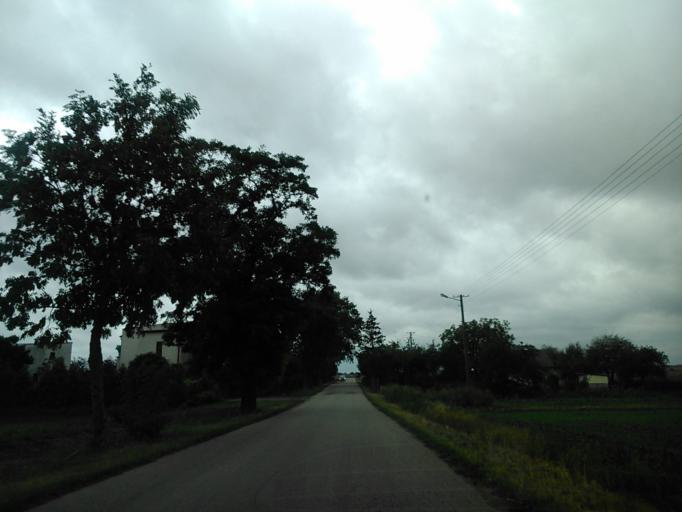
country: PL
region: Kujawsko-Pomorskie
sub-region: Powiat inowroclawski
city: Inowroclaw
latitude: 52.7621
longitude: 18.3178
